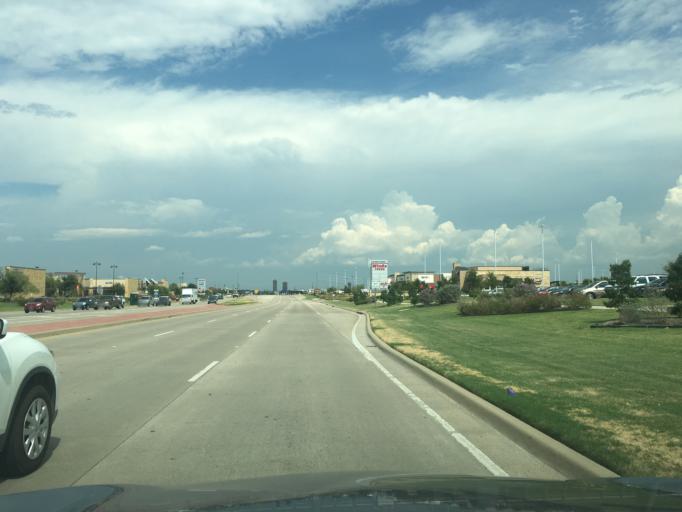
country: US
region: Texas
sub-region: Denton County
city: Denton
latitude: 33.2297
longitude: -97.1686
